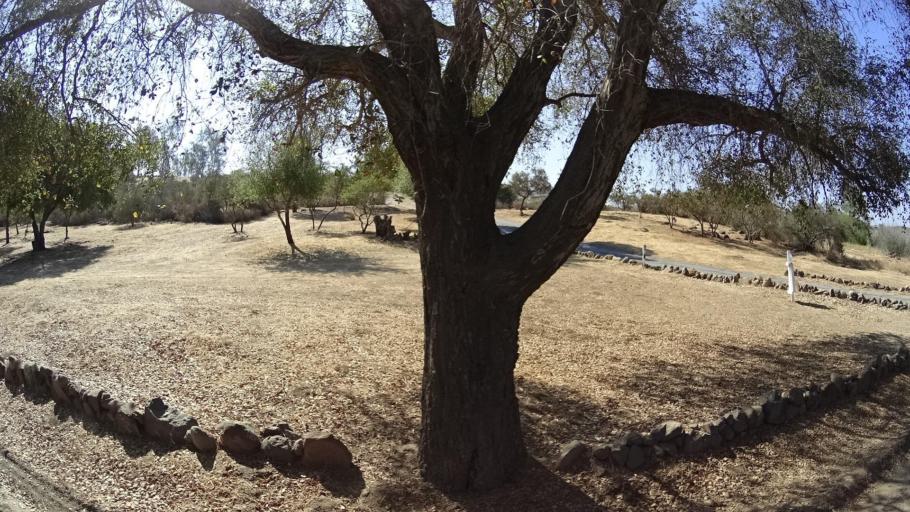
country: US
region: California
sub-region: San Diego County
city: Fallbrook
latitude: 33.4165
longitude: -117.2113
